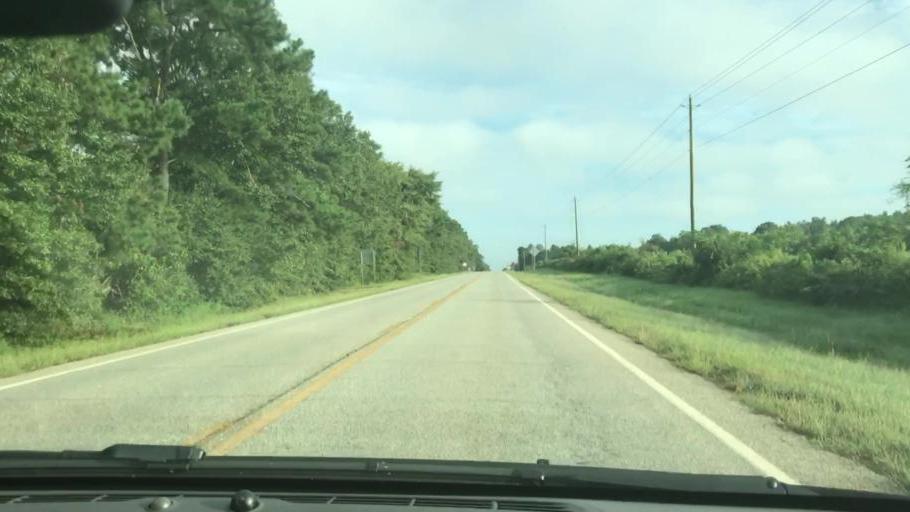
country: US
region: Georgia
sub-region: Clay County
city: Fort Gaines
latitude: 31.7228
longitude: -85.0444
